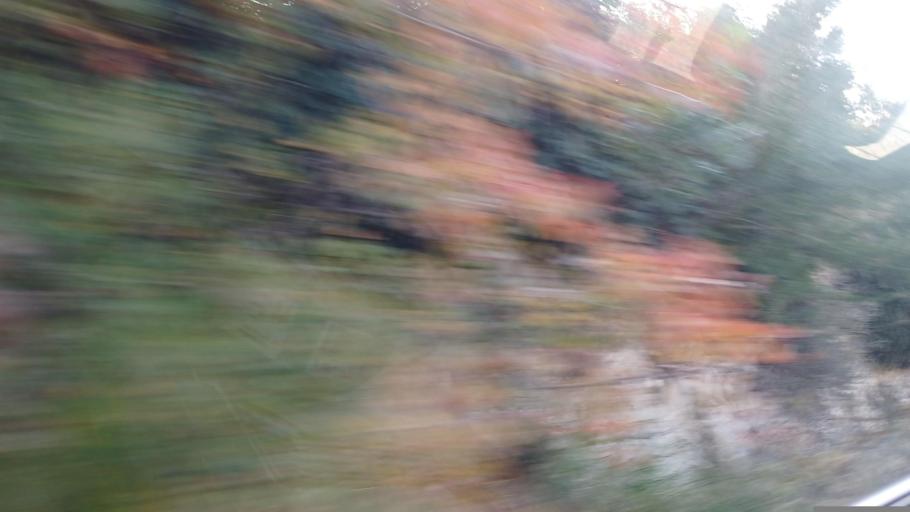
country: CY
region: Larnaka
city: Kofinou
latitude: 34.8388
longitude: 33.3050
